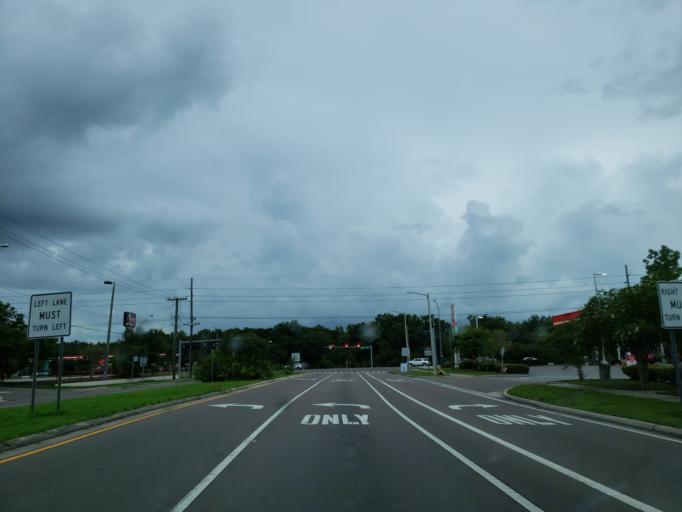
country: US
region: Florida
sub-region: Hillsborough County
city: Ruskin
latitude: 27.7142
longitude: -82.3942
